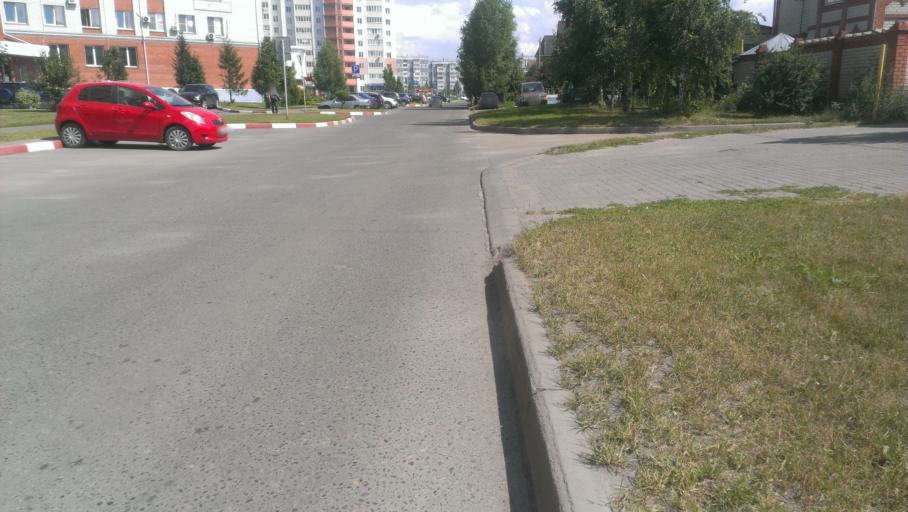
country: RU
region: Altai Krai
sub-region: Gorod Barnaulskiy
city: Barnaul
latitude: 53.3565
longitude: 83.6917
